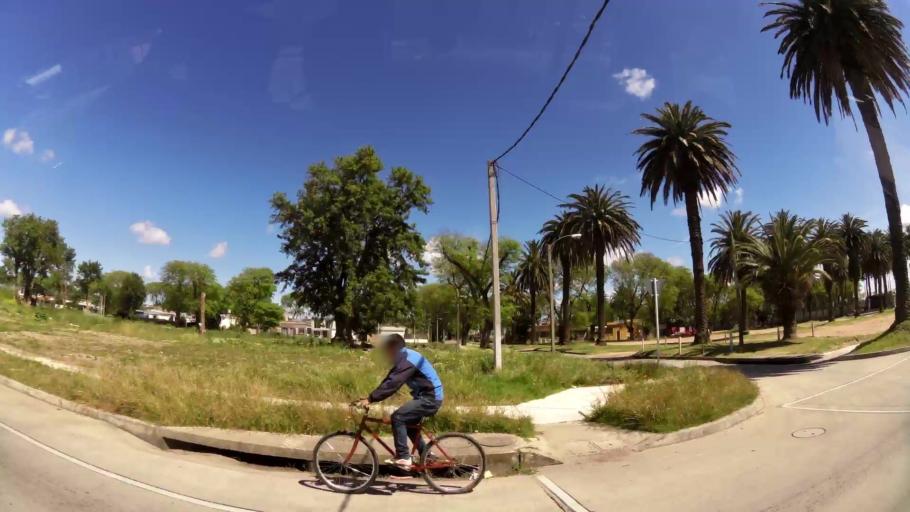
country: UY
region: Montevideo
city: Montevideo
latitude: -34.8433
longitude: -56.1432
